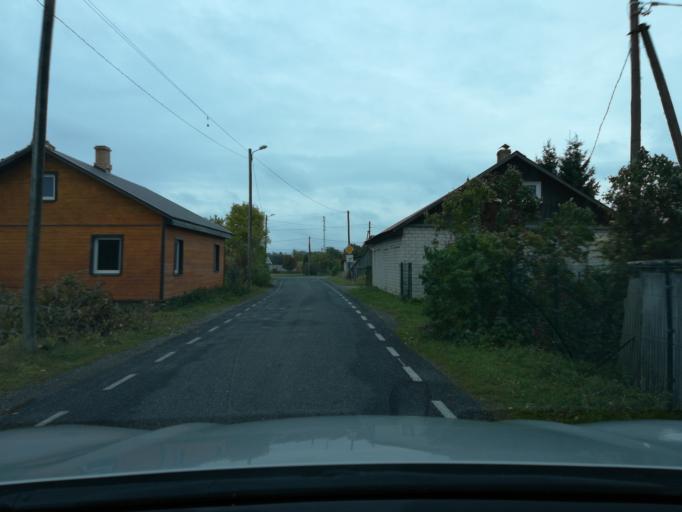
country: EE
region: Ida-Virumaa
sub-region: Johvi vald
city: Johvi
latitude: 59.0112
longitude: 27.4250
